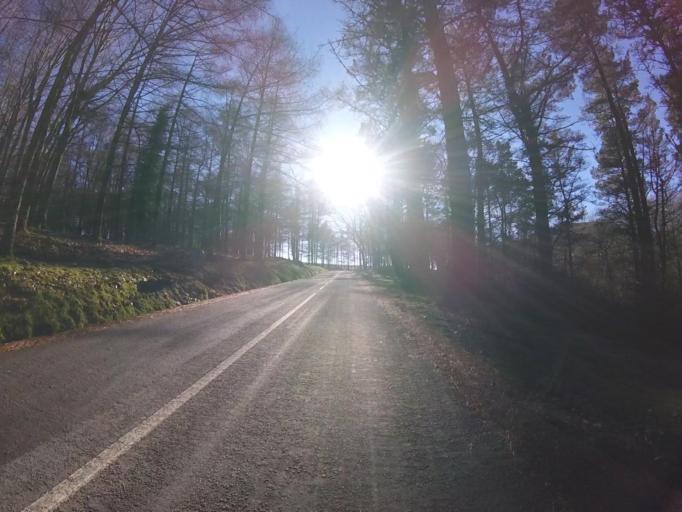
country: ES
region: Basque Country
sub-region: Provincia de Guipuzcoa
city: Irun
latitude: 43.3079
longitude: -1.7554
